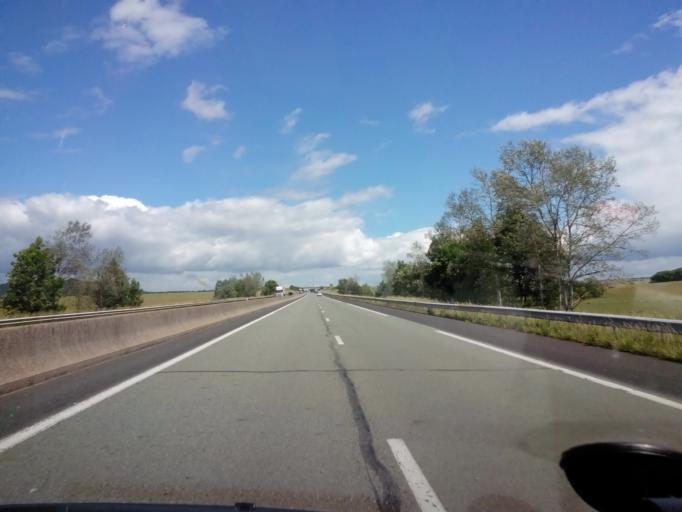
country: FR
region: Lorraine
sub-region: Departement des Vosges
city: Lamarche
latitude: 48.1655
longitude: 5.7101
